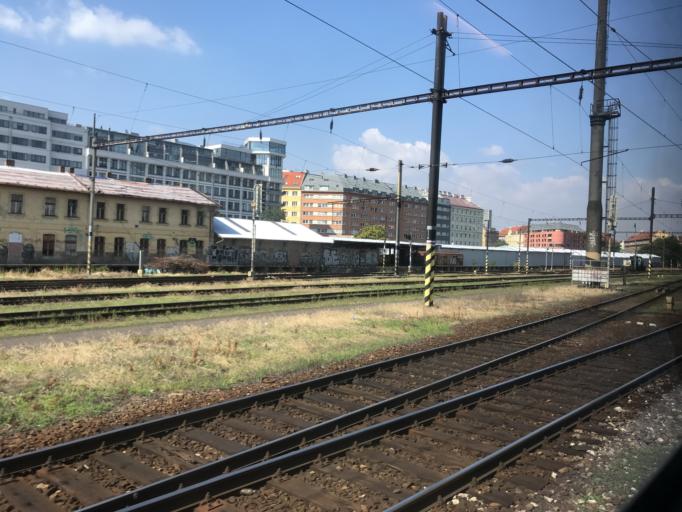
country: CZ
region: Praha
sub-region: Praha 8
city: Karlin
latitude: 50.0633
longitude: 14.4519
